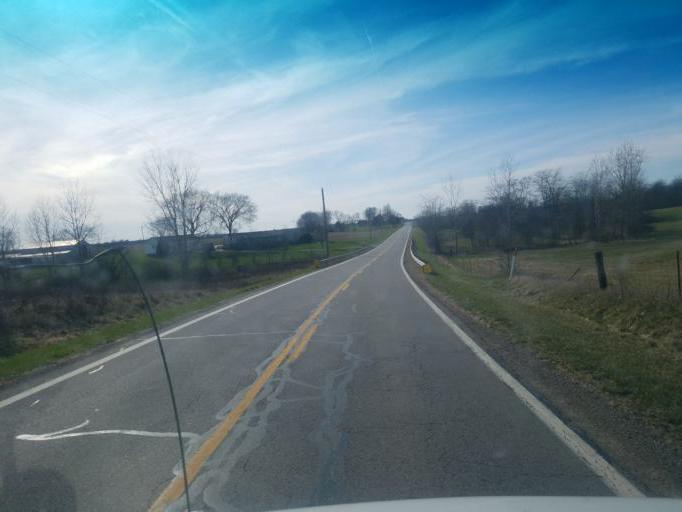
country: US
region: Ohio
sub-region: Champaign County
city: North Lewisburg
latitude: 40.3414
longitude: -83.4891
